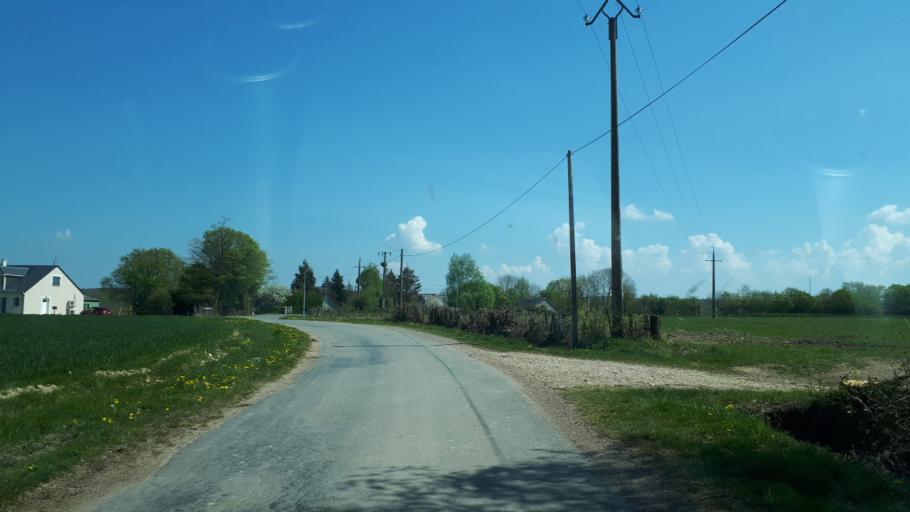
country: FR
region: Centre
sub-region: Departement du Cher
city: Henrichemont
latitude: 47.3038
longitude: 2.5606
